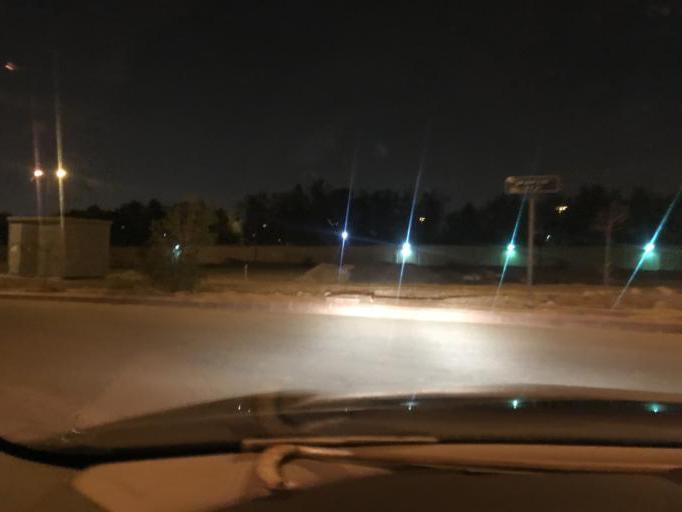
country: SA
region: Ar Riyad
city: Riyadh
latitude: 24.8160
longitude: 46.7163
